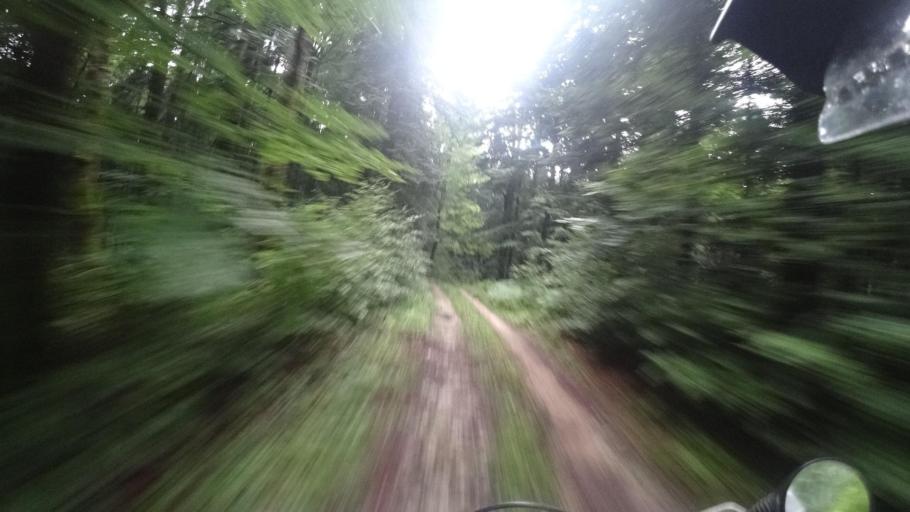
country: HR
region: Licko-Senjska
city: Jezerce
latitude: 44.8063
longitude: 15.6400
